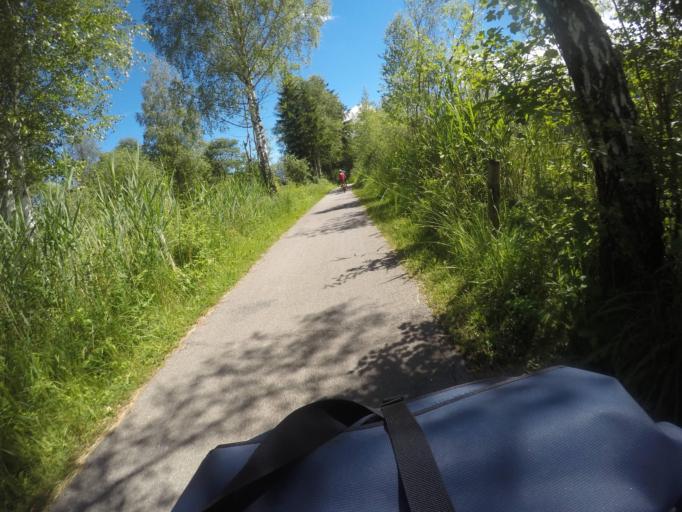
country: DE
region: Bavaria
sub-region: Swabia
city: Schwangau
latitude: 47.5875
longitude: 10.7608
